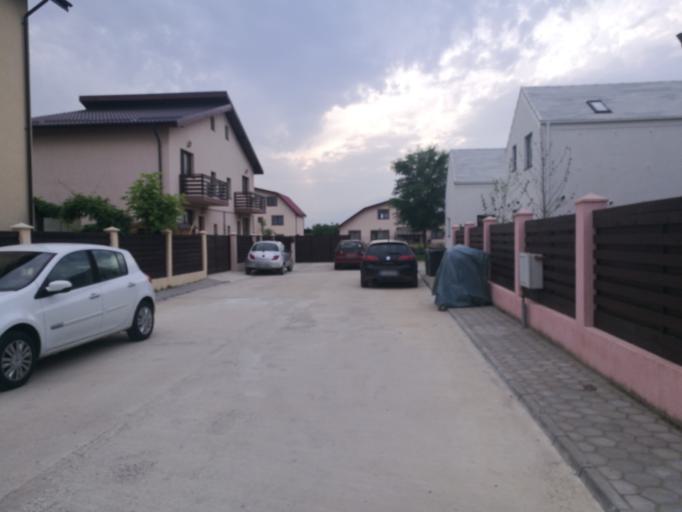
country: RO
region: Ilfov
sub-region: Comuna Vidra
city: Vidra
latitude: 44.2771
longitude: 26.1844
